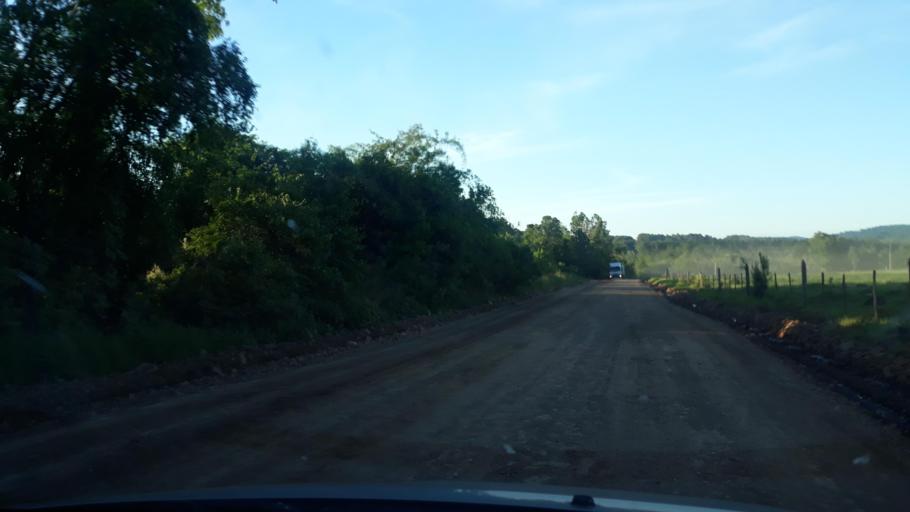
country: AR
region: Misiones
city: Ruiz de Montoya
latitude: -27.0486
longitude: -55.0039
